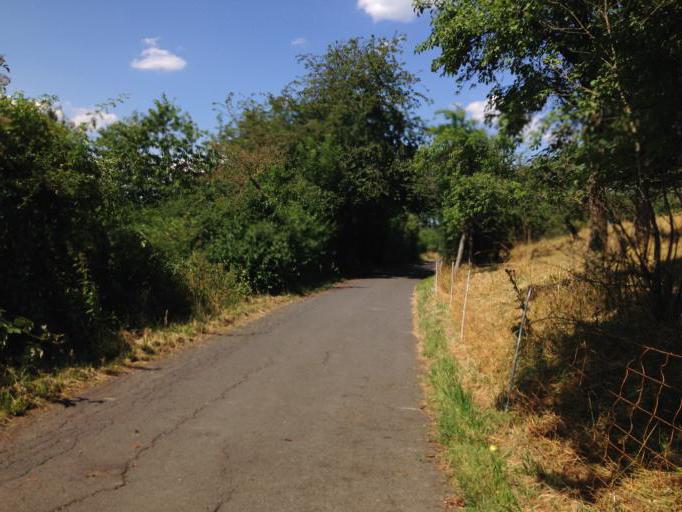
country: DE
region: Hesse
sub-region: Regierungsbezirk Giessen
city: Heuchelheim
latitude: 50.6150
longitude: 8.6315
